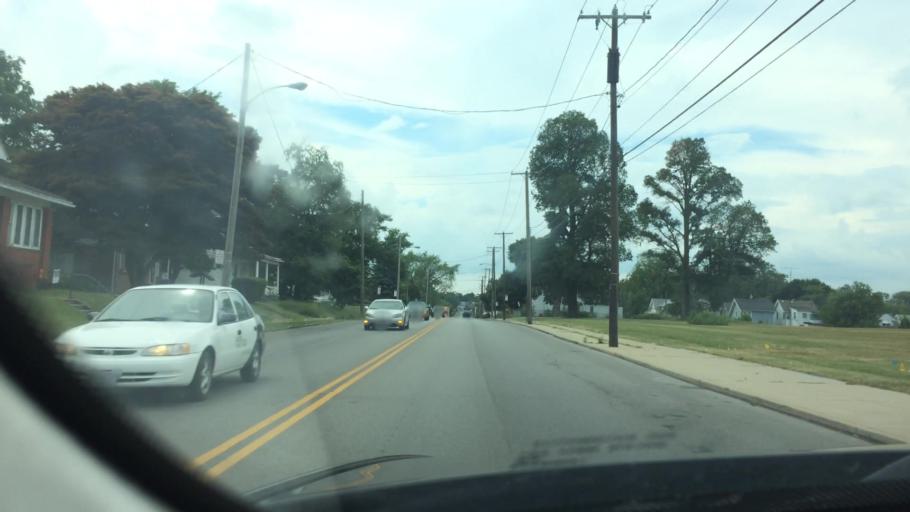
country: US
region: Ohio
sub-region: Wood County
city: Rossford
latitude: 41.6347
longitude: -83.5703
